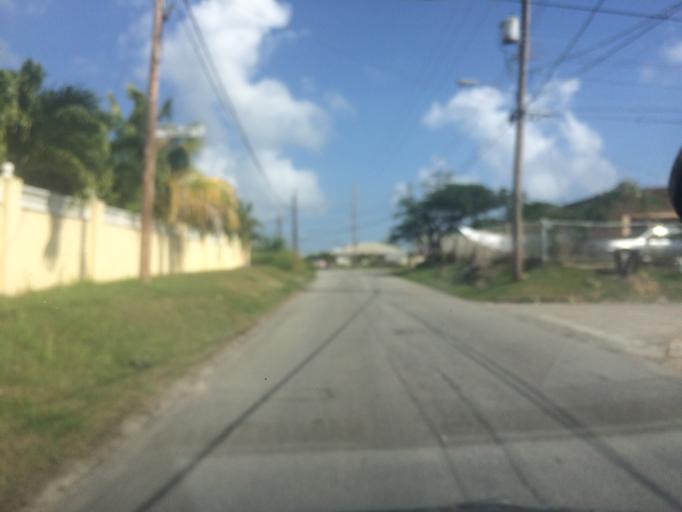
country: BB
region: Christ Church
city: Oistins
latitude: 13.0579
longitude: -59.5147
